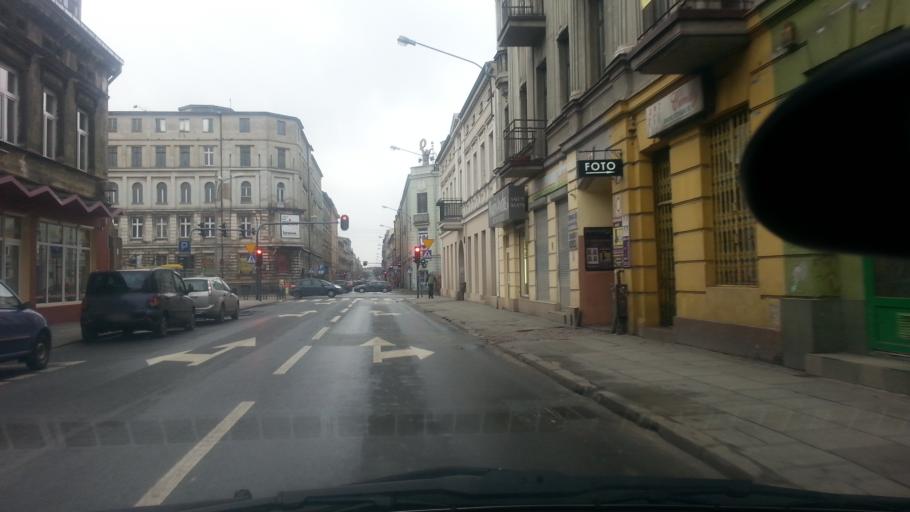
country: PL
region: Lodz Voivodeship
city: Lodz
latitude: 51.7725
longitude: 19.4541
